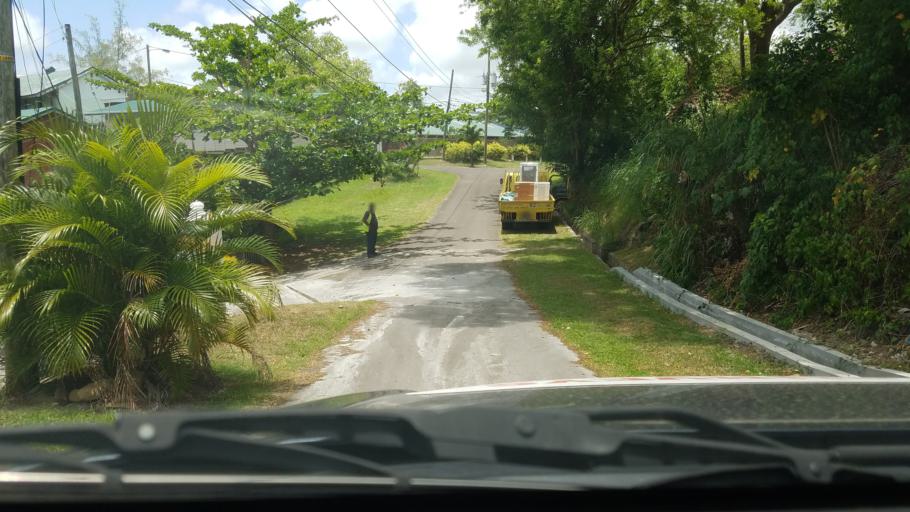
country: LC
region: Castries Quarter
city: Bisee
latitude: 14.0238
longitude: -61.0005
